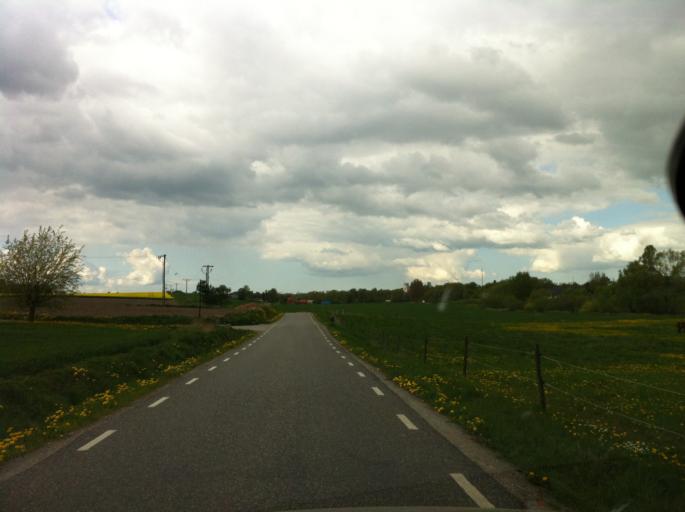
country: SE
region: Skane
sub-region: Svalovs Kommun
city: Teckomatorp
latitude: 55.8737
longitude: 13.0091
